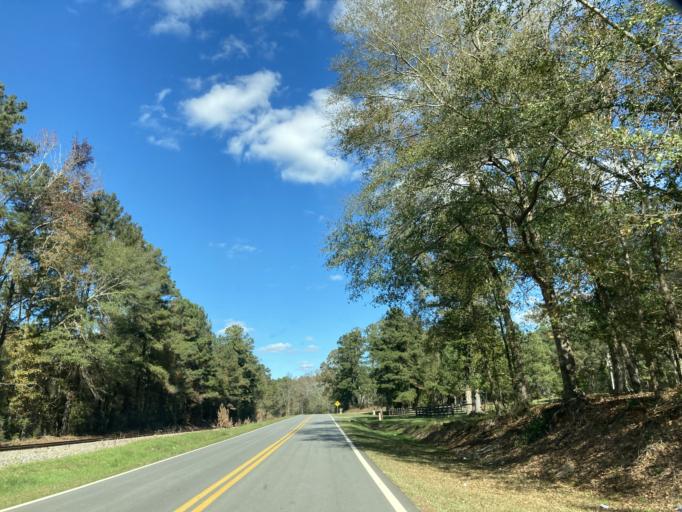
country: US
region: Georgia
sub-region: Jones County
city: Gray
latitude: 32.9504
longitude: -83.5158
